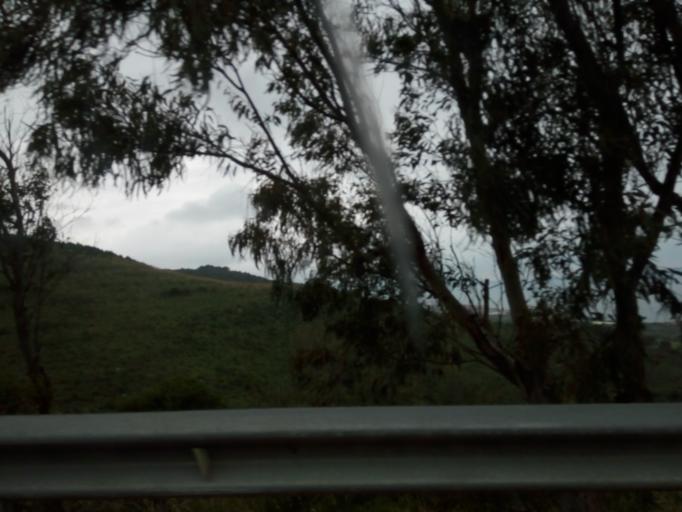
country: DZ
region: Tipaza
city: Tipasa
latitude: 36.5840
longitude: 2.5421
